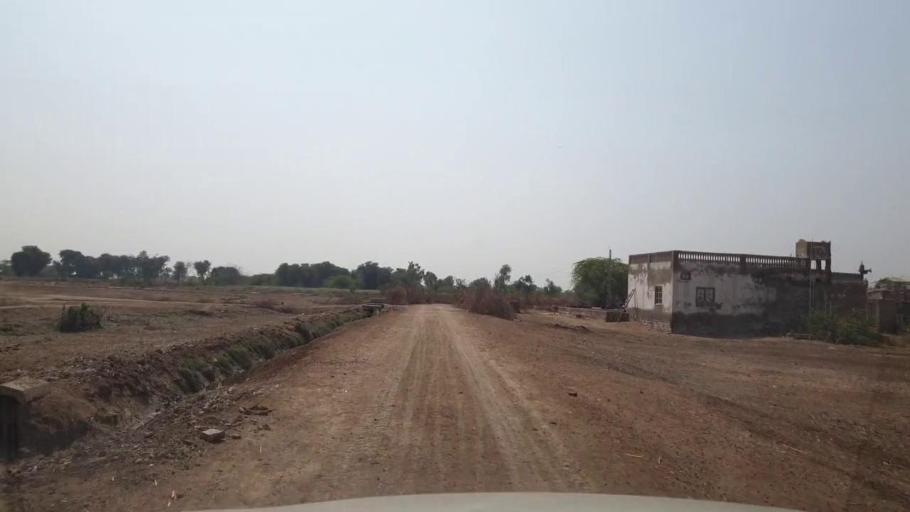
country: PK
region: Sindh
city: Chor
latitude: 25.4536
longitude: 69.6796
